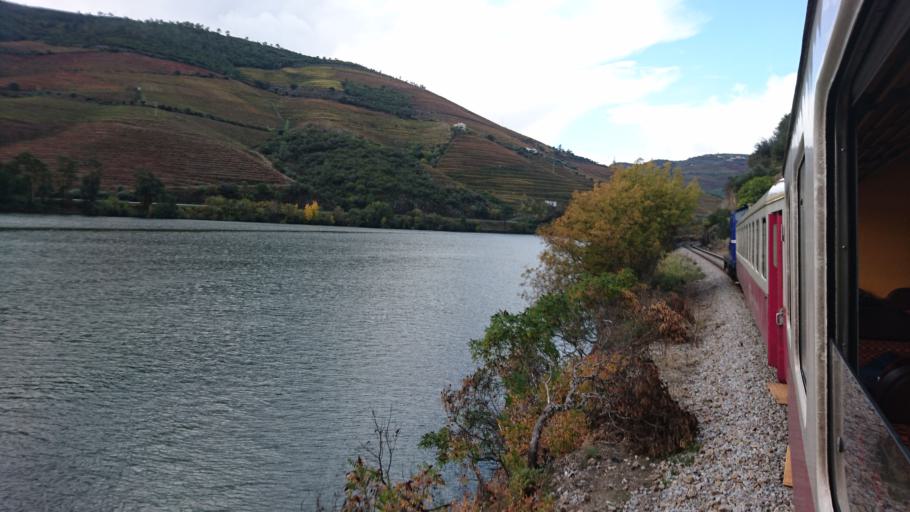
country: PT
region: Vila Real
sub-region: Sabrosa
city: Vilela
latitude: 41.1614
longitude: -7.6249
